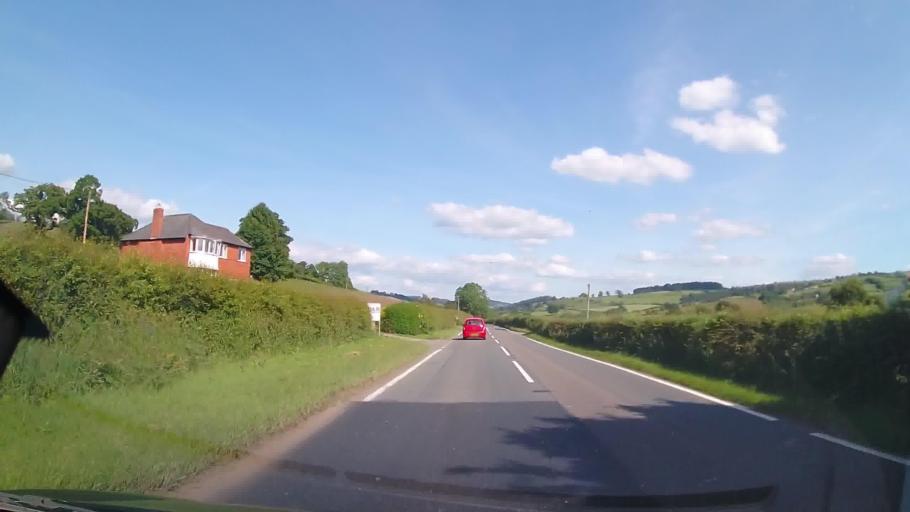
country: GB
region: Wales
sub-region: Sir Powys
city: Llanfyllin
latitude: 52.6654
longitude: -3.2991
